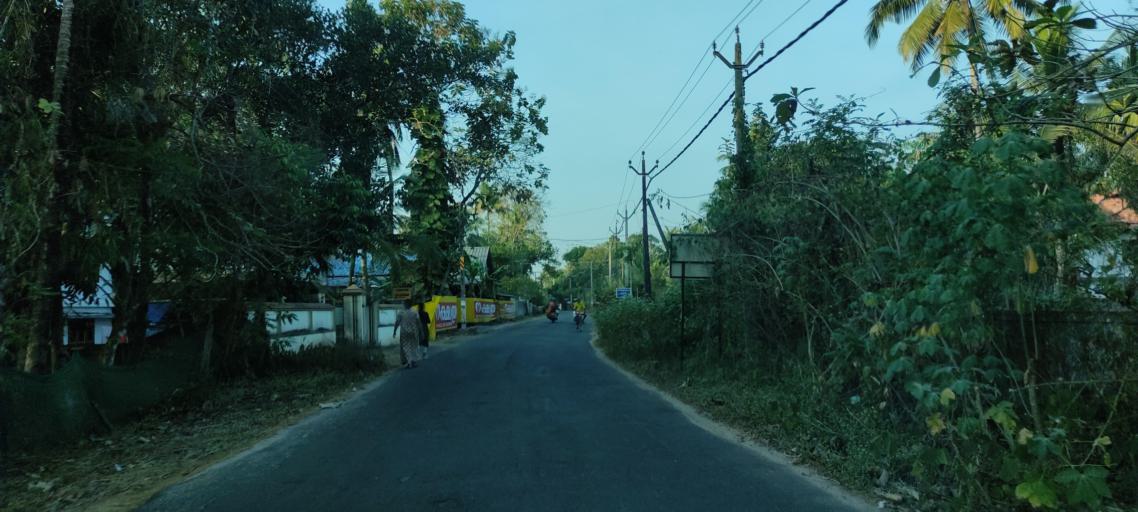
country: IN
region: Kerala
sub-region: Alappuzha
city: Kutiatodu
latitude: 9.7626
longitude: 76.3533
